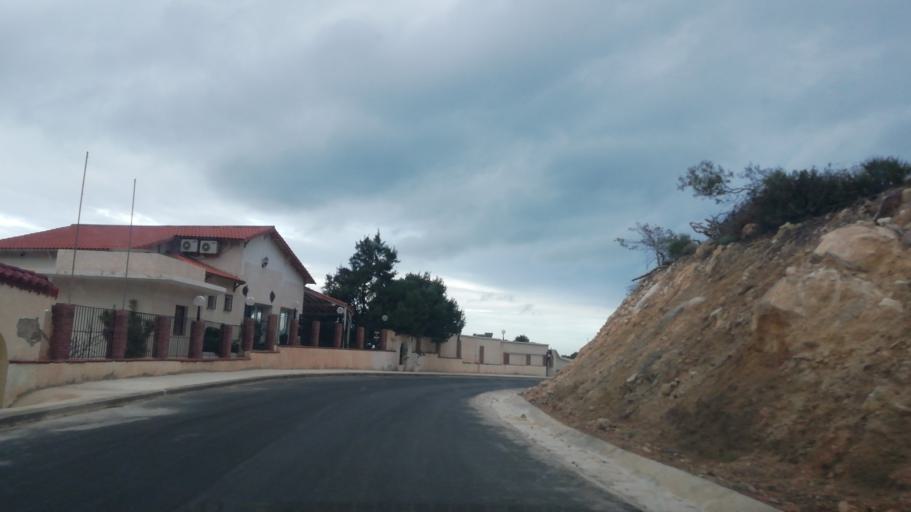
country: DZ
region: Oran
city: Bir el Djir
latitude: 35.7807
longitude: -0.5099
